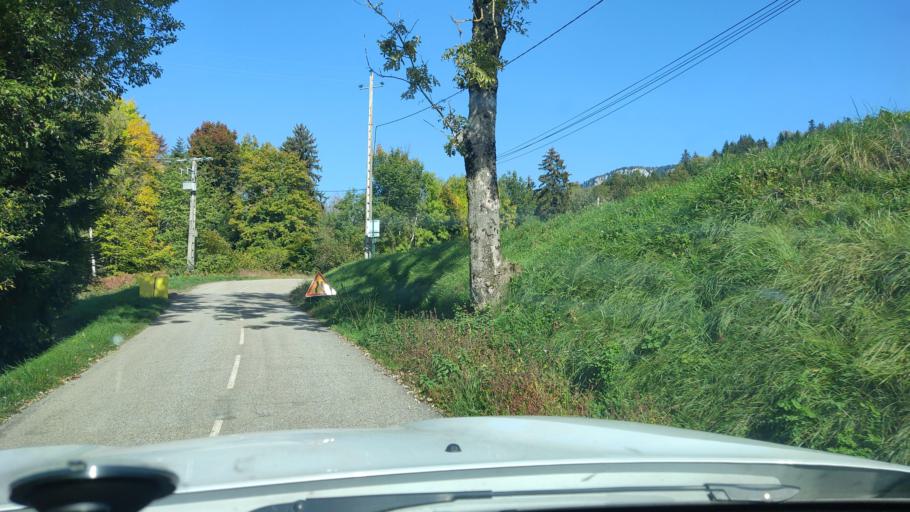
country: FR
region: Rhone-Alpes
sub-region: Departement de la Savoie
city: Les Echelles
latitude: 45.4640
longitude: 5.7630
